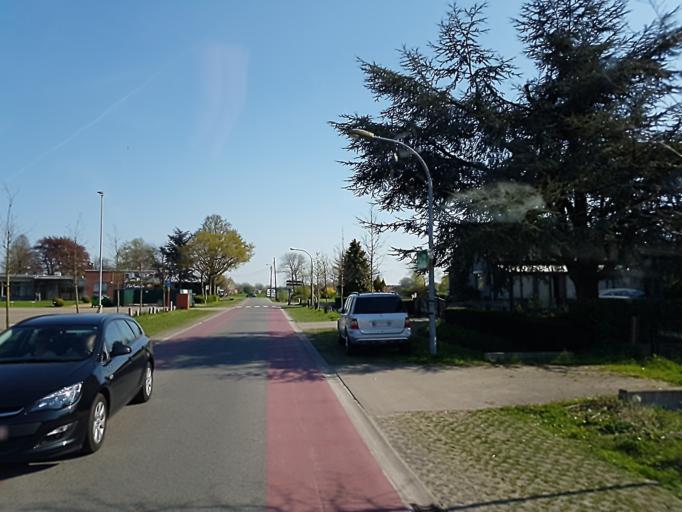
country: BE
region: Flanders
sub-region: Provincie Oost-Vlaanderen
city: Sint-Niklaas
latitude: 51.1695
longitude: 4.1862
